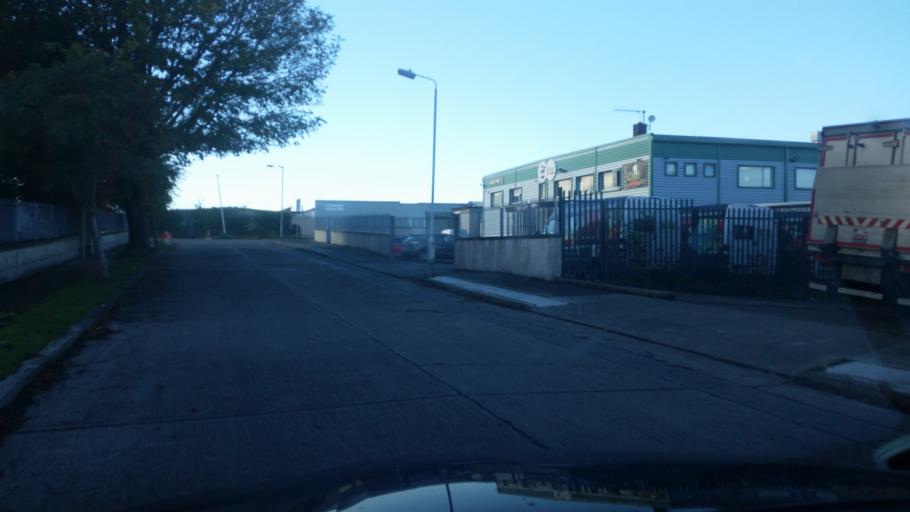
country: IE
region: Leinster
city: Cabra
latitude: 53.3743
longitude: -6.2951
